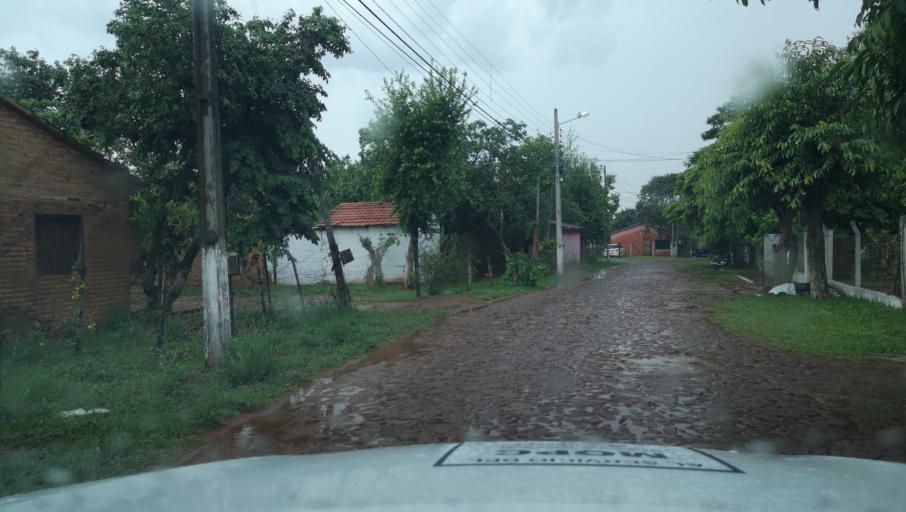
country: PY
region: Misiones
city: Santa Maria
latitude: -26.8976
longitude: -57.0332
